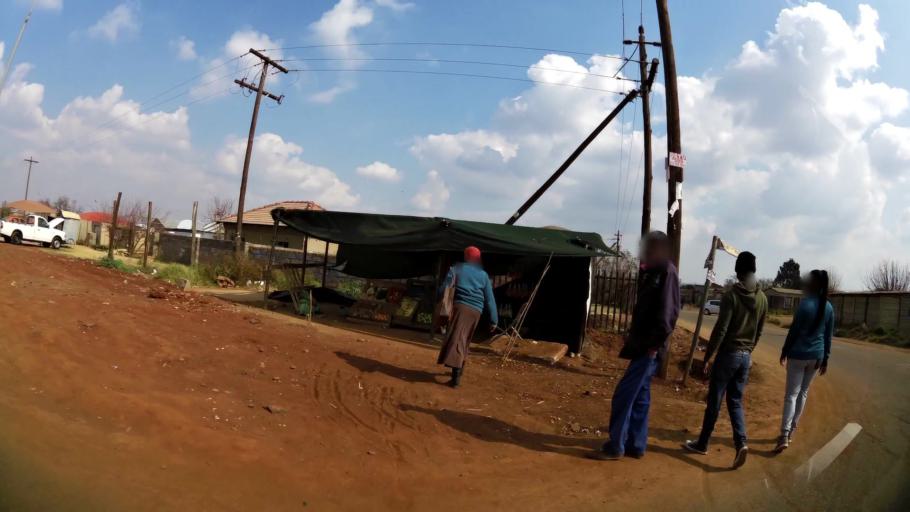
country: ZA
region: Gauteng
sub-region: Ekurhuleni Metropolitan Municipality
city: Springs
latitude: -26.1312
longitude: 28.4768
